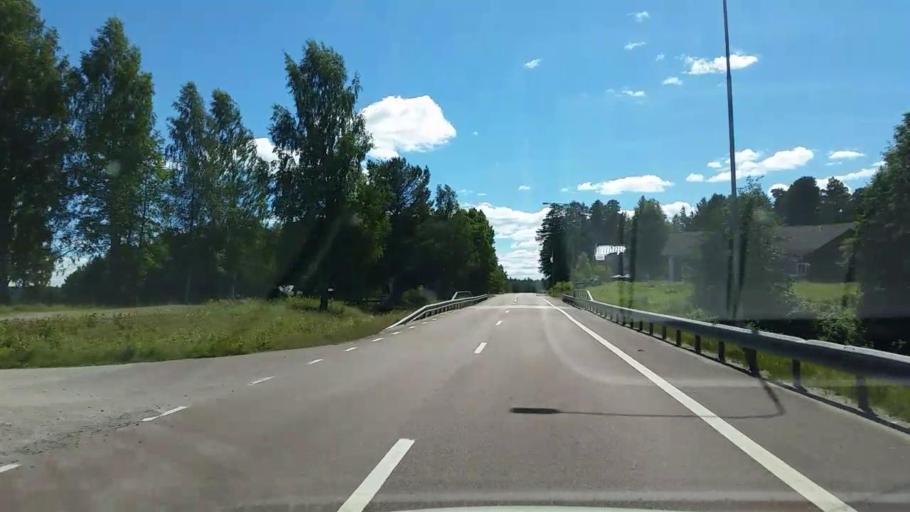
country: SE
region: Gaevleborg
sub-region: Bollnas Kommun
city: Vittsjo
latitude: 61.0448
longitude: 15.7942
